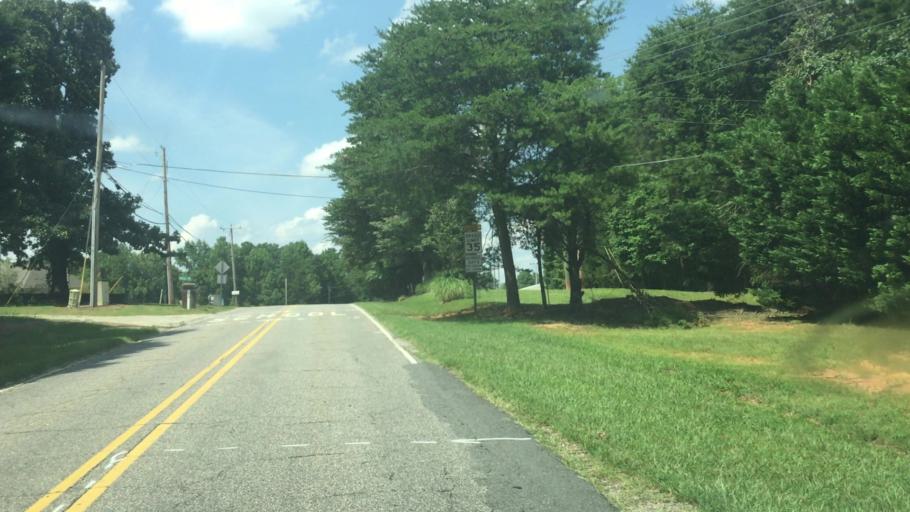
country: US
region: North Carolina
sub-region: Iredell County
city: Mooresville
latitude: 35.5517
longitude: -80.7907
